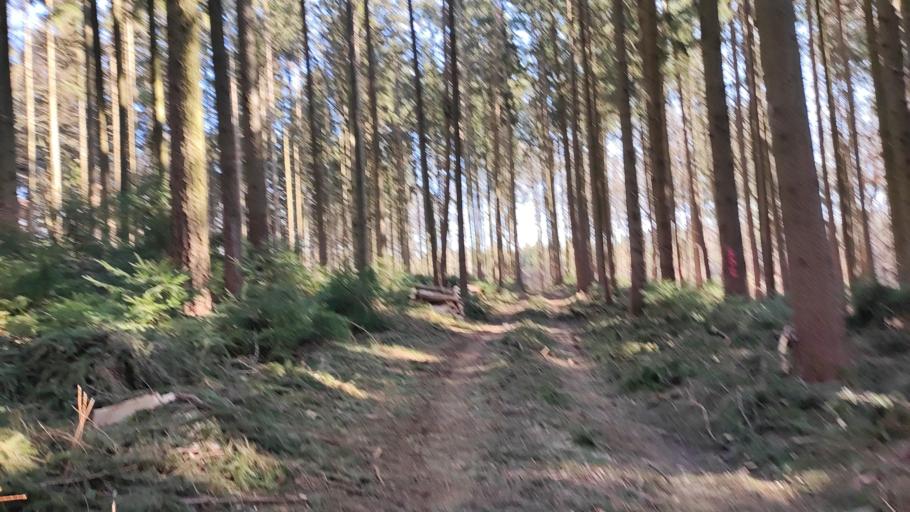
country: DE
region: Bavaria
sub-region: Swabia
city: Zusmarshausen
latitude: 48.4321
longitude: 10.6072
